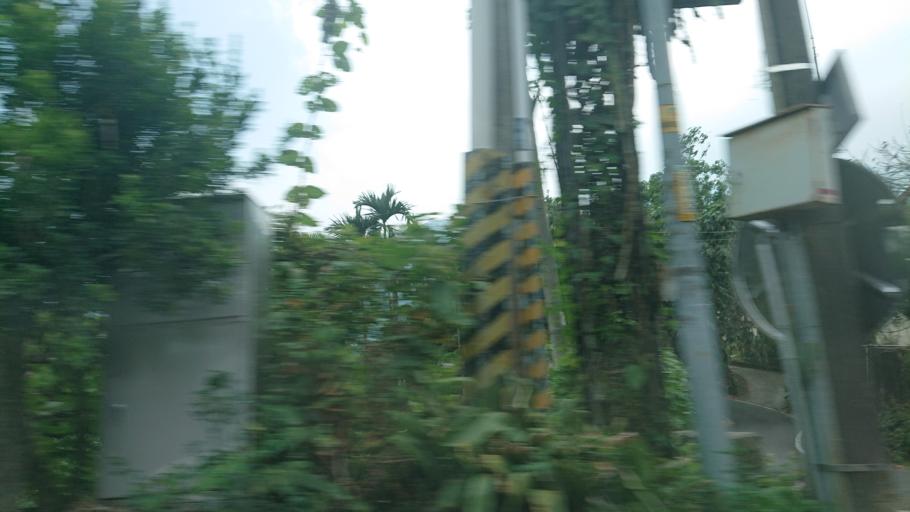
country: TW
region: Taiwan
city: Lugu
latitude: 23.5828
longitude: 120.6950
